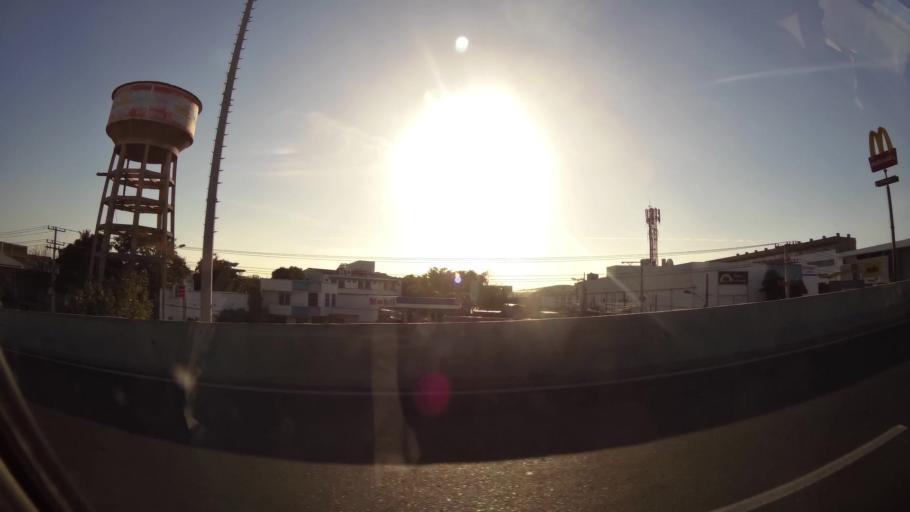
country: CO
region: Atlantico
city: Soledad
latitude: 10.9259
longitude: -74.7784
